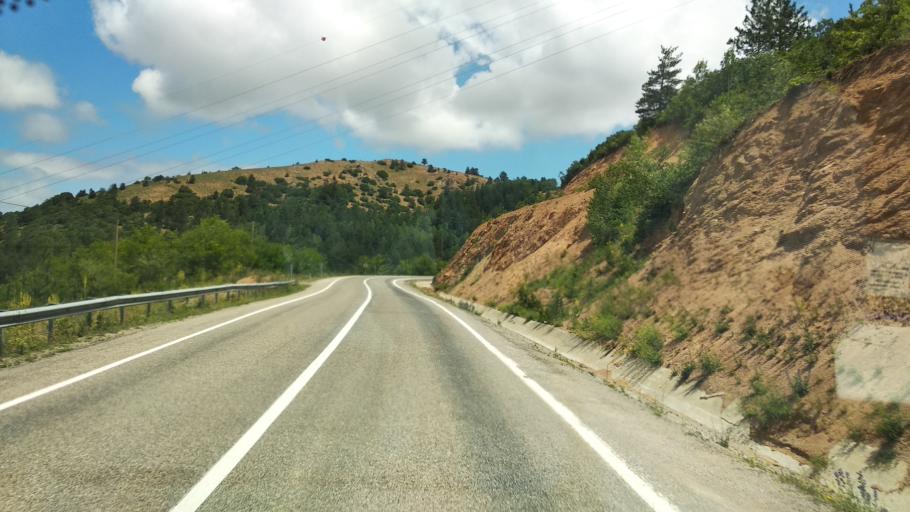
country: TR
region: Gumushane
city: Kose
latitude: 40.2980
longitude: 39.5704
